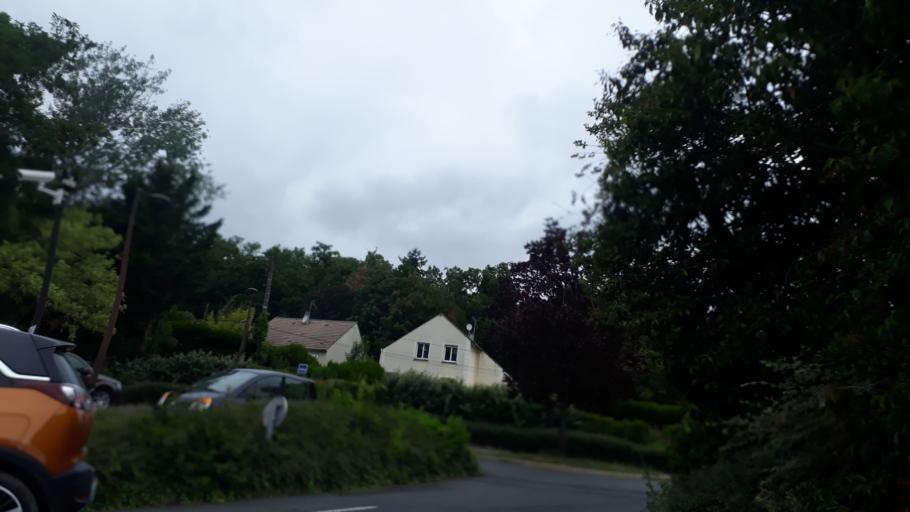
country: FR
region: Ile-de-France
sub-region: Departement de l'Essonne
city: La Ville-du-Bois
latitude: 48.6712
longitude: 2.2770
